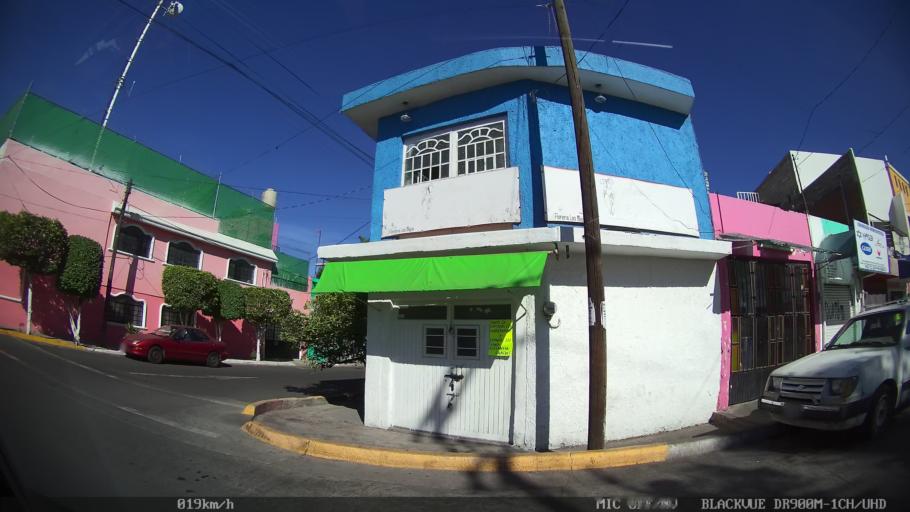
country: MX
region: Jalisco
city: Tlaquepaque
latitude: 20.6900
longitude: -103.2782
